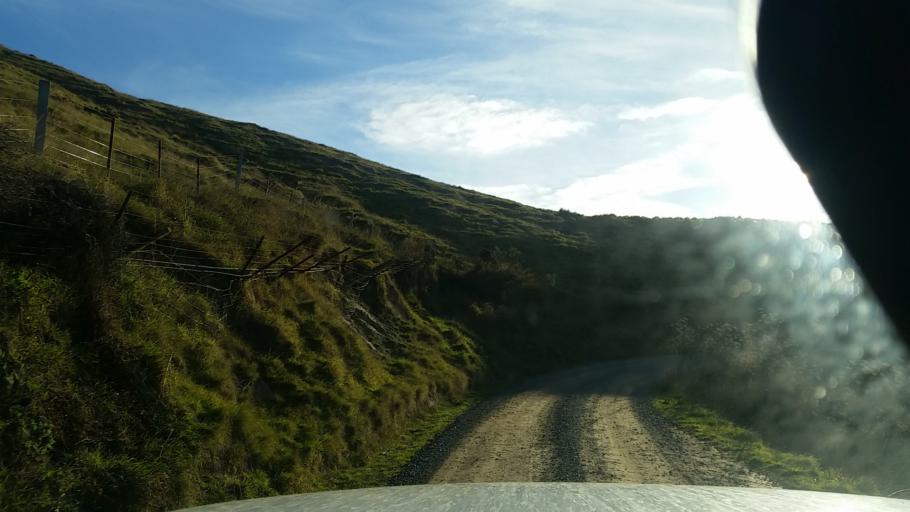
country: NZ
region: Canterbury
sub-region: Christchurch City
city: Christchurch
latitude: -43.6188
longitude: 172.7766
